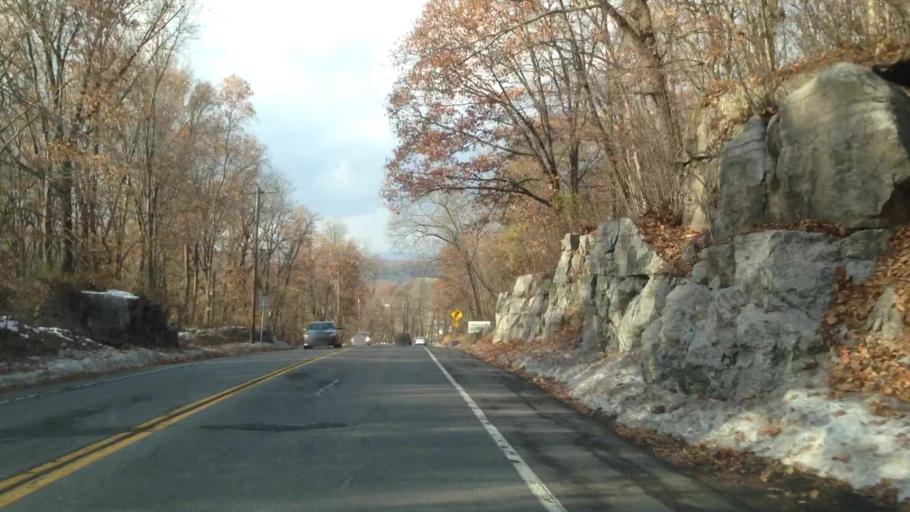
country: US
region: New York
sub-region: Ulster County
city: Lincoln Park
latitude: 41.9428
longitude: -73.9889
